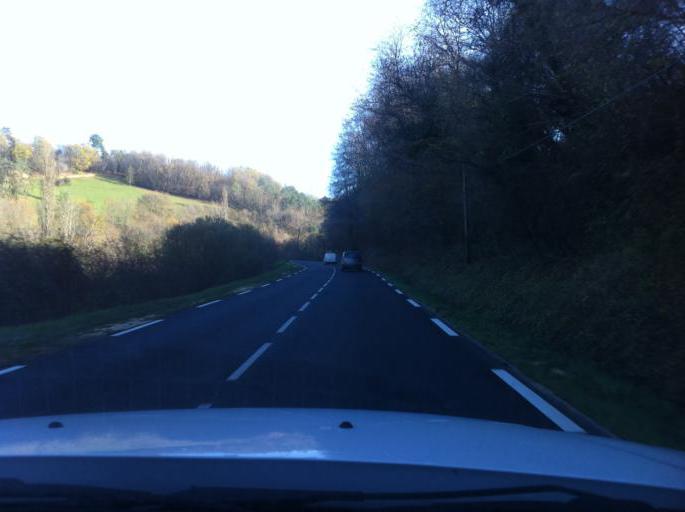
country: FR
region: Aquitaine
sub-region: Departement de la Dordogne
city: Rouffignac-Saint-Cernin-de-Reilhac
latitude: 45.0346
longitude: 0.8989
